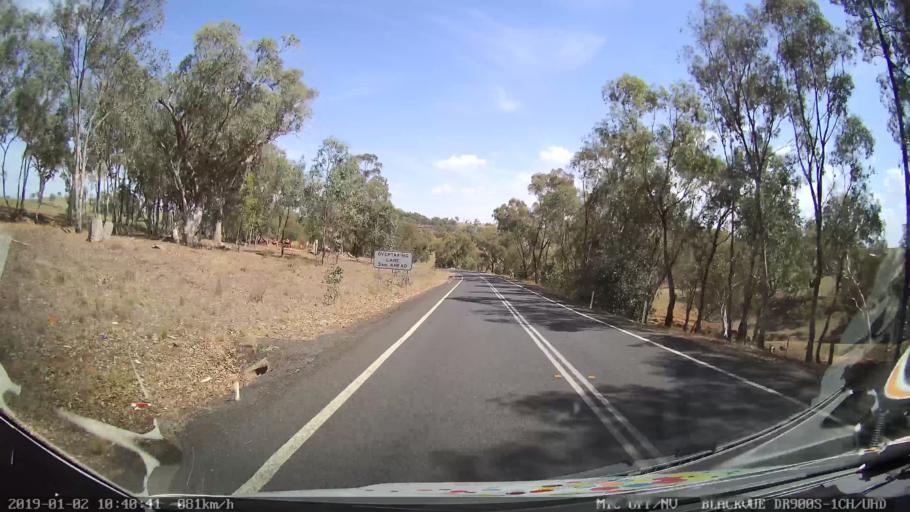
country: AU
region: New South Wales
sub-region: Cootamundra
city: Cootamundra
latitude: -34.7996
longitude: 148.3140
